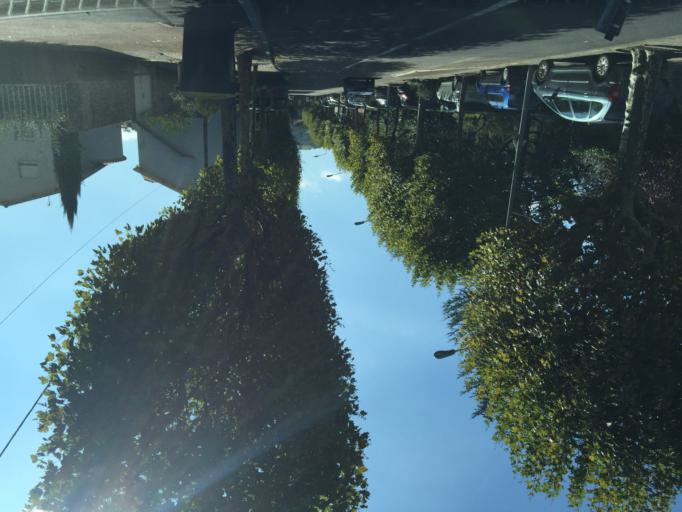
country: FR
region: Rhone-Alpes
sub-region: Departement de la Loire
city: Saint-Chamond
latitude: 45.4685
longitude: 4.5175
